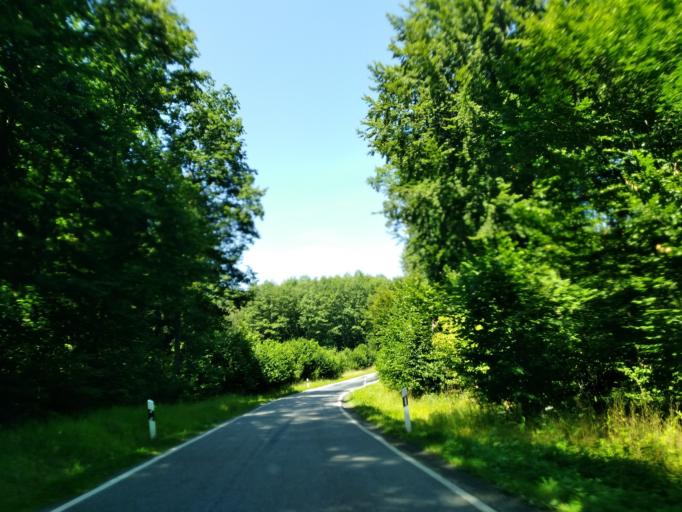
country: DE
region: Baden-Wuerttemberg
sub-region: Regierungsbezirk Stuttgart
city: Roigheim
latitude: 49.3828
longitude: 9.3007
